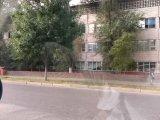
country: KZ
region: Almaty Qalasy
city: Almaty
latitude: 43.2699
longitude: 76.9359
